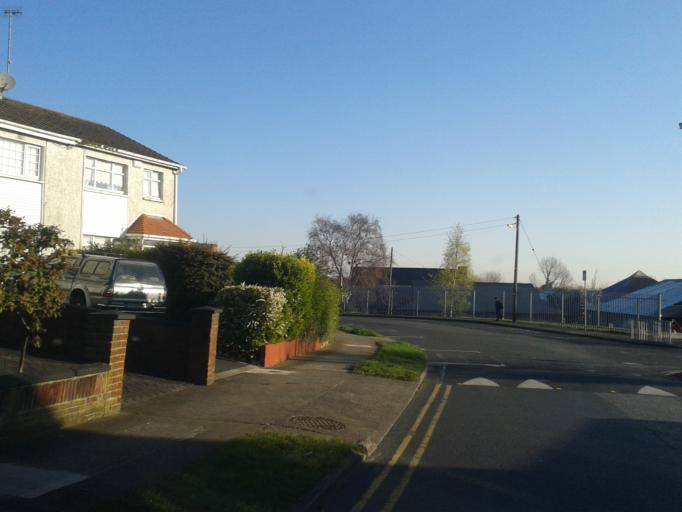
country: IE
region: Leinster
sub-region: Fingal County
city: Swords
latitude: 53.4568
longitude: -6.2149
